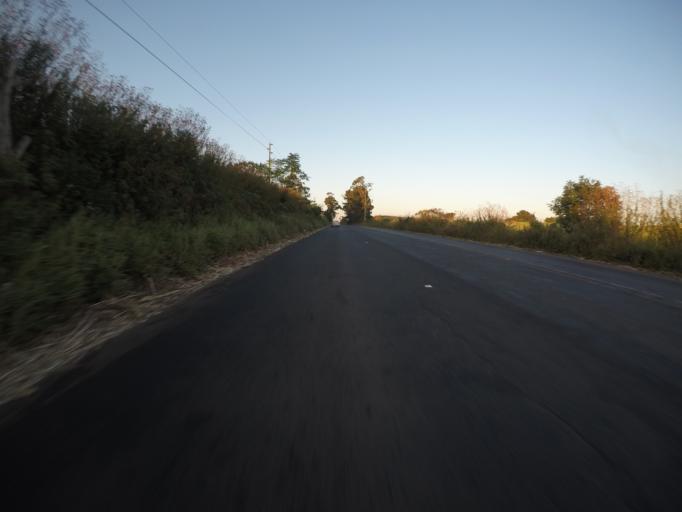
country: ZA
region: KwaZulu-Natal
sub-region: uThungulu District Municipality
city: Empangeni
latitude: -28.7982
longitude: 31.8956
